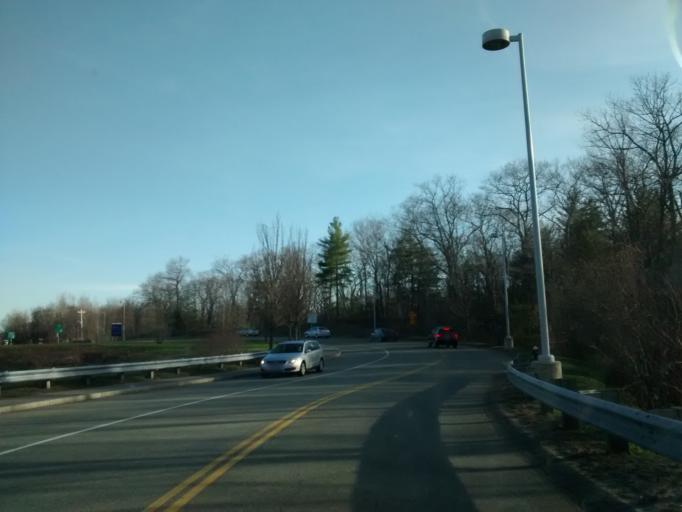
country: US
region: Massachusetts
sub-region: Norfolk County
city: Avon
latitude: 42.1363
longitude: -71.0688
